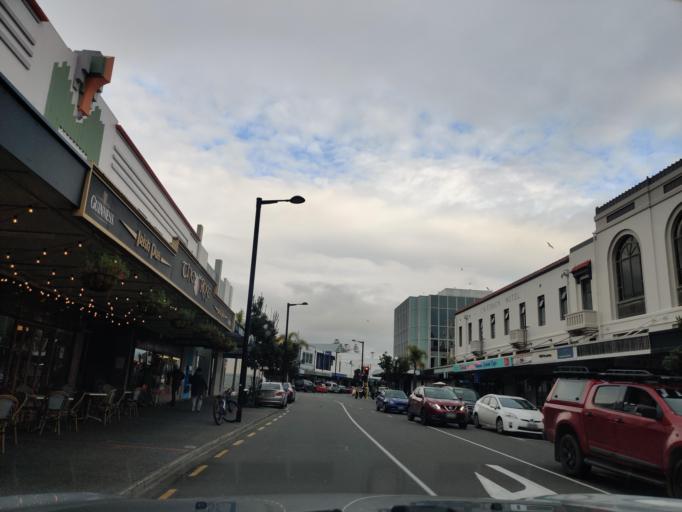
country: NZ
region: Hawke's Bay
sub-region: Napier City
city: Napier
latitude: -39.4896
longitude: 176.9182
